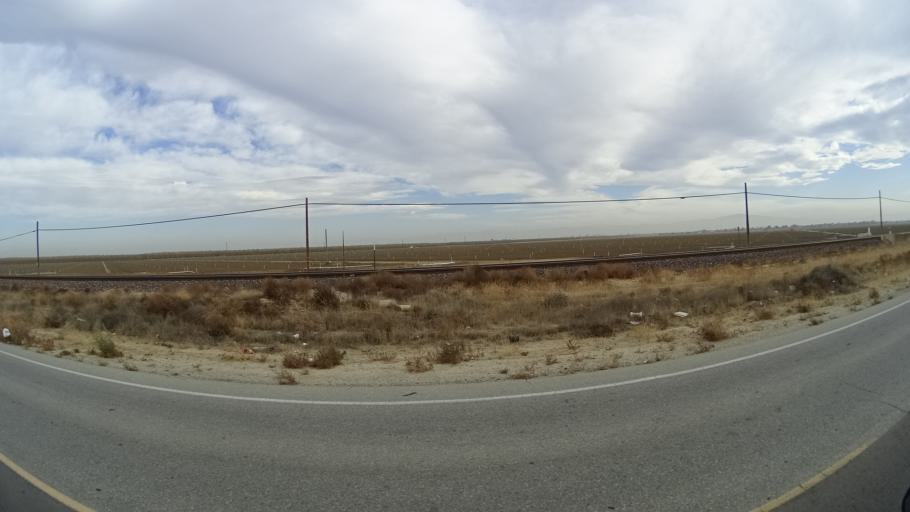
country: US
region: California
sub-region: Kern County
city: Rosedale
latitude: 35.4163
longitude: -119.1683
